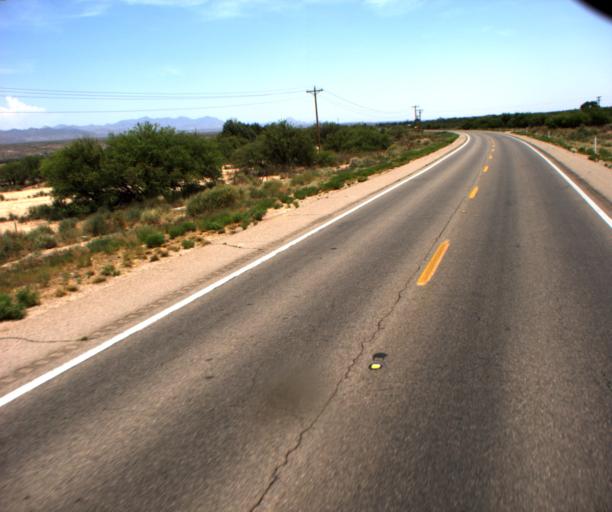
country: US
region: Arizona
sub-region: Graham County
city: Bylas
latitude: 33.0428
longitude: -109.9798
